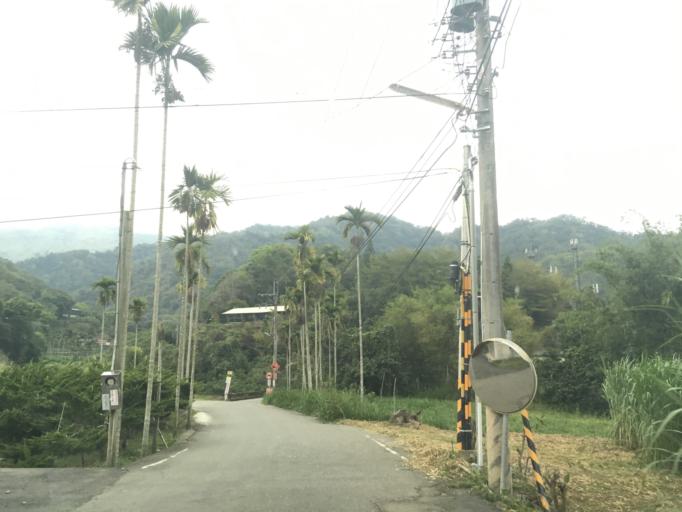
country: TW
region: Taiwan
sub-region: Nantou
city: Puli
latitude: 23.9492
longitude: 120.8676
